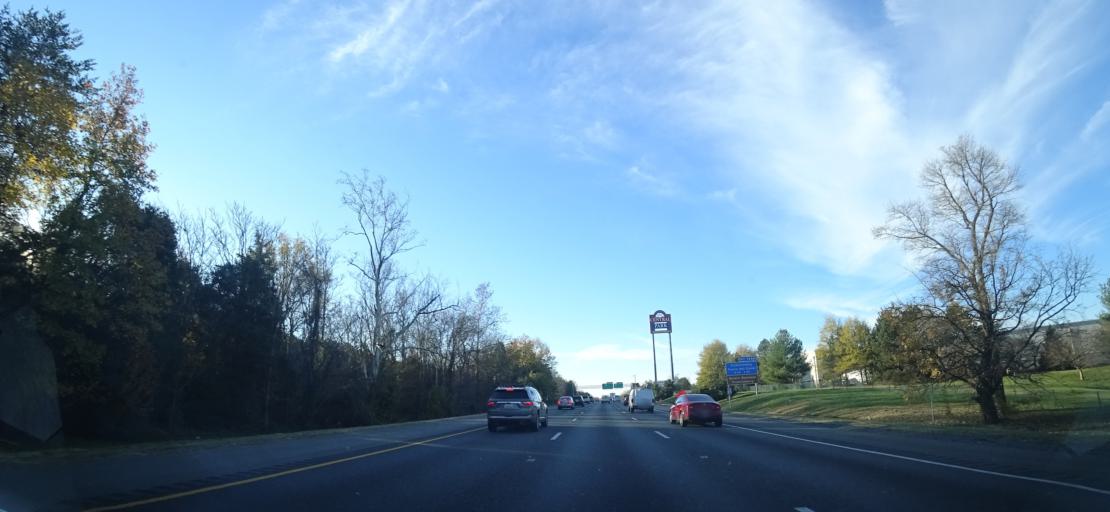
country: US
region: Virginia
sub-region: Stafford County
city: Falmouth
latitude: 38.3040
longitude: -77.5031
